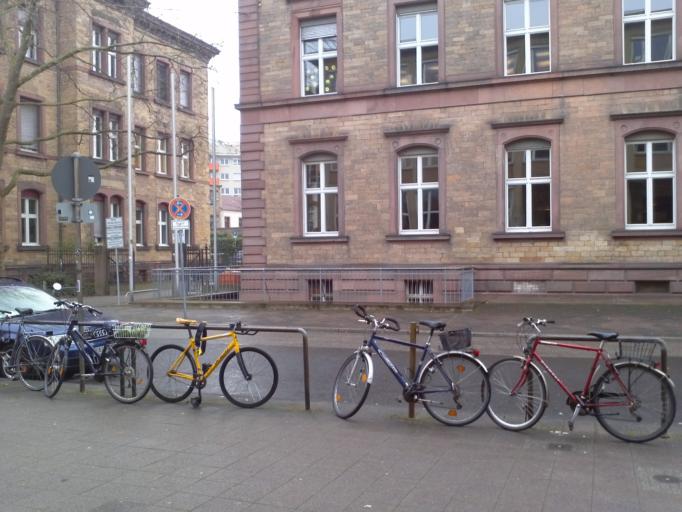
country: DE
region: Baden-Wuerttemberg
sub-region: Karlsruhe Region
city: Karlsruhe
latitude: 49.0108
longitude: 8.4107
